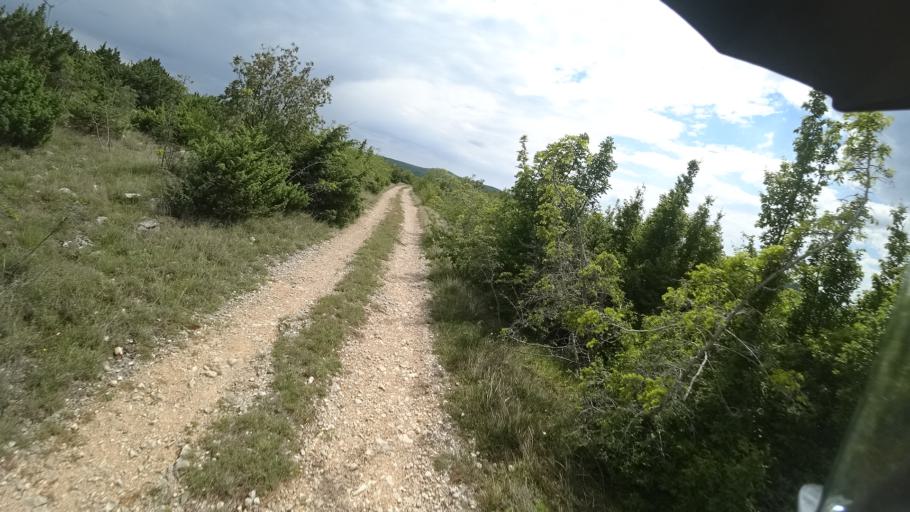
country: HR
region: Sibensko-Kniniska
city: Kistanje
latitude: 44.0914
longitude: 16.0498
